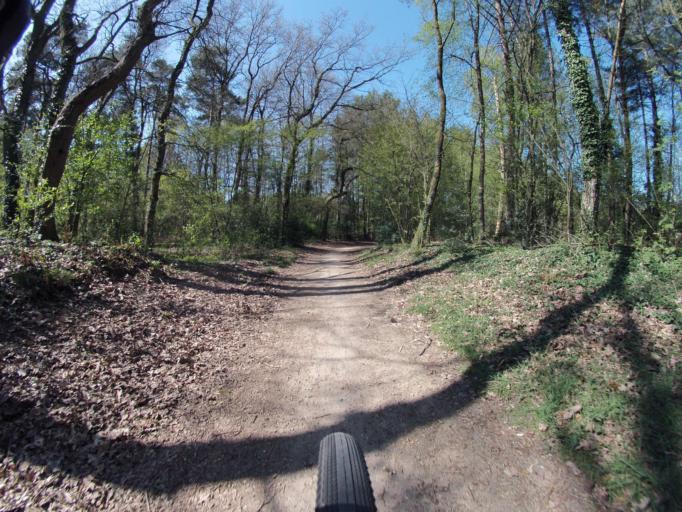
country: NL
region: Overijssel
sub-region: Gemeente Losser
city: Losser
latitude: 52.2802
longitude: 7.0327
